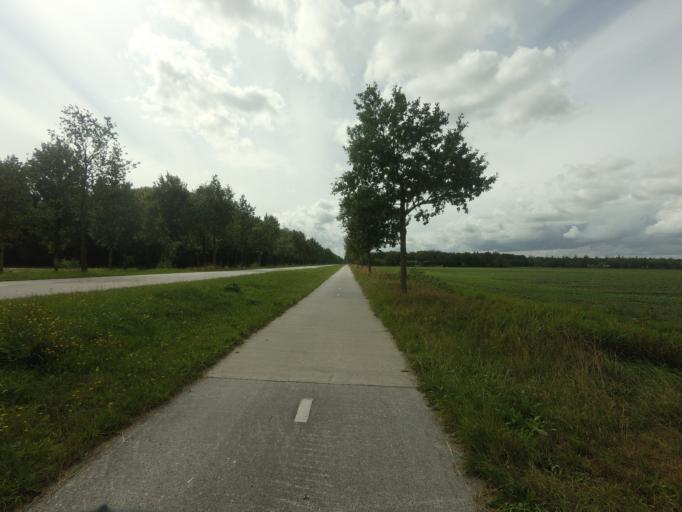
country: NL
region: Groningen
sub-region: Gemeente Leek
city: Leek
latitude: 53.0281
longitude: 6.4165
